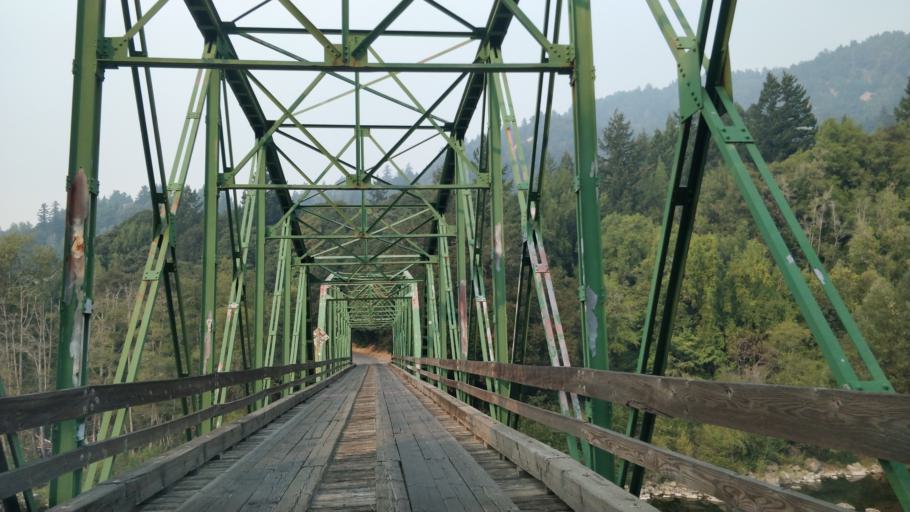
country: US
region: California
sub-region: Humboldt County
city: Rio Dell
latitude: 40.2436
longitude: -124.1231
